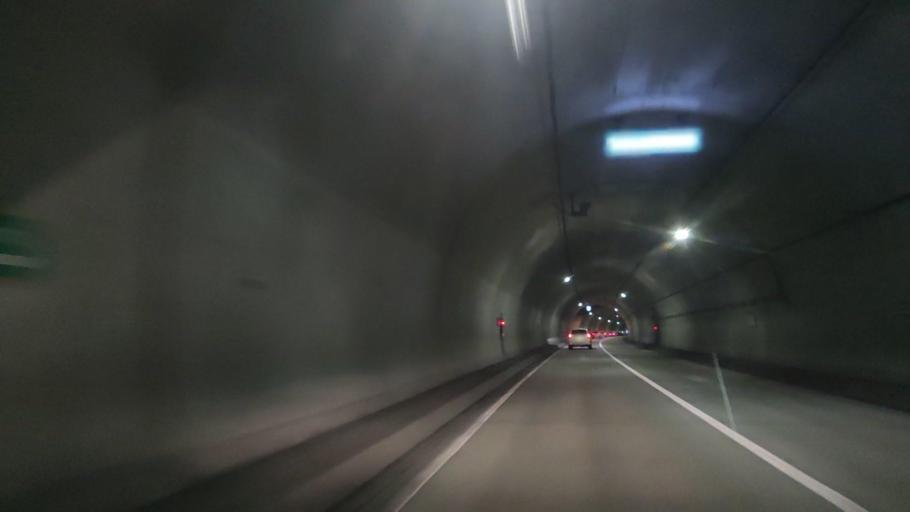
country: JP
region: Hokkaido
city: Ishikari
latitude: 43.5261
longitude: 141.3937
